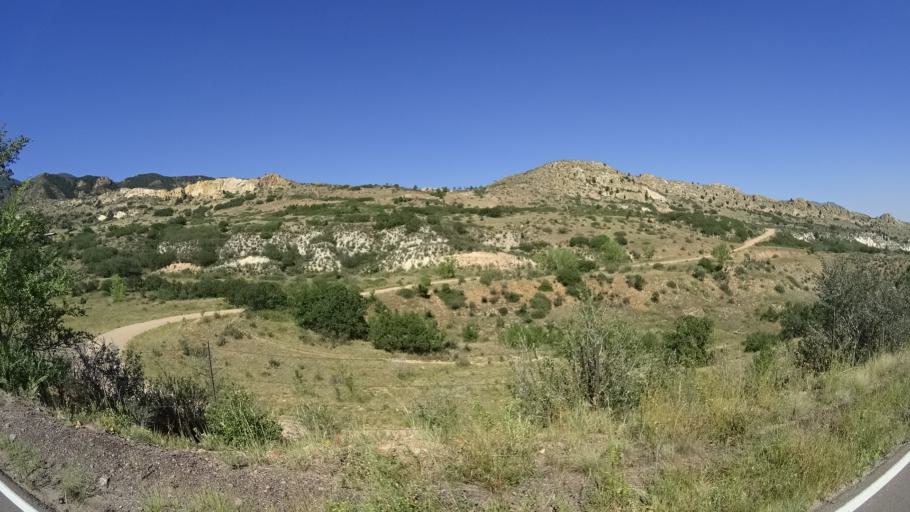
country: US
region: Colorado
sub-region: El Paso County
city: Manitou Springs
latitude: 38.8327
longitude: -104.8779
